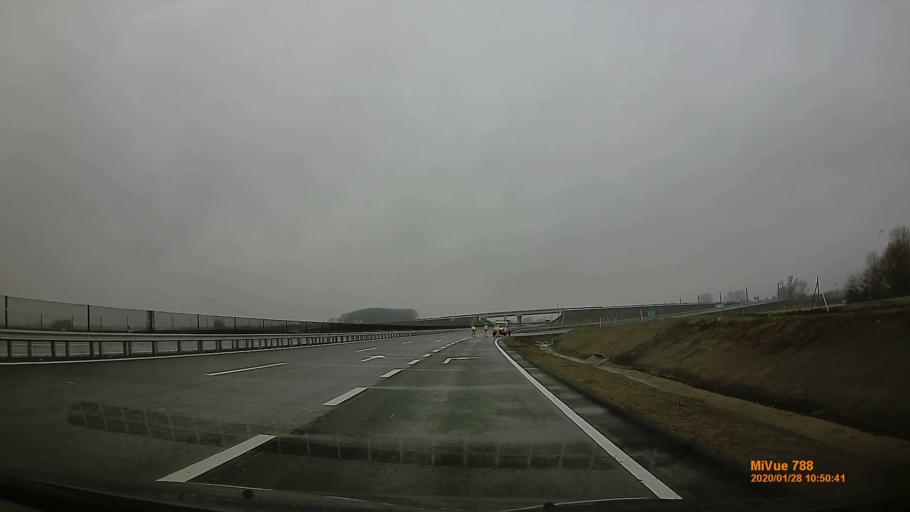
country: HU
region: Pest
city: Peteri
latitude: 47.3725
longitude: 19.4261
